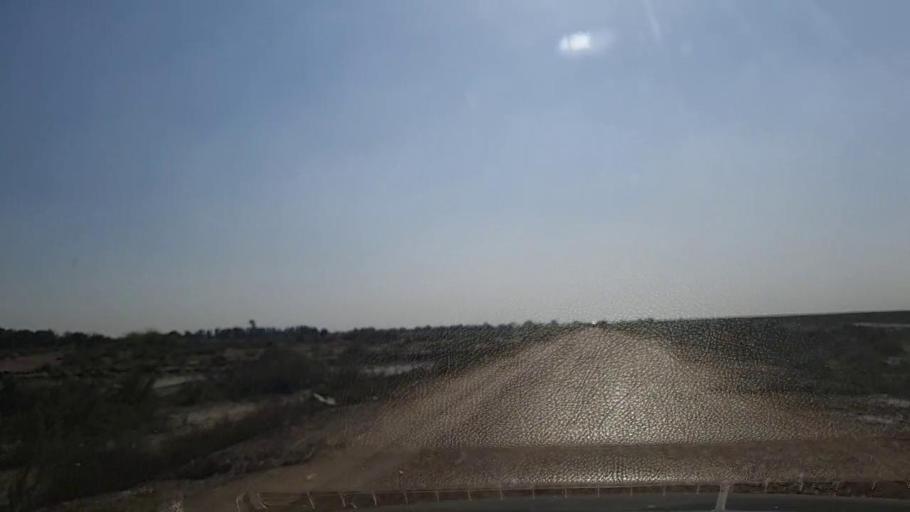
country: PK
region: Sindh
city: Daro Mehar
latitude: 24.7616
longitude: 68.0646
